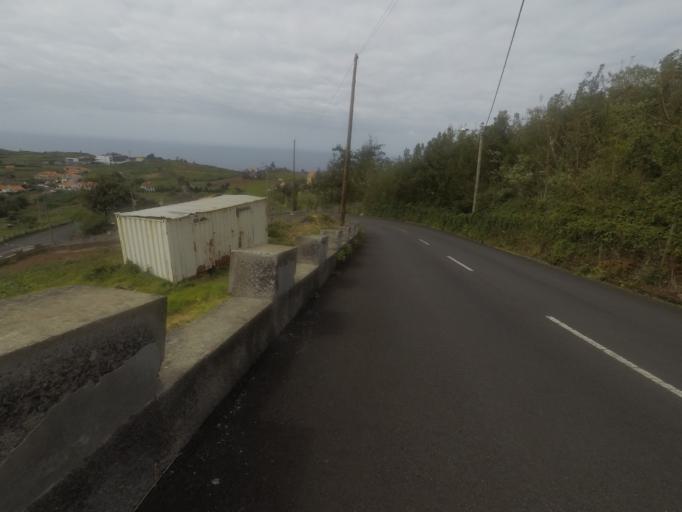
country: PT
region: Madeira
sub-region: Santana
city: Santana
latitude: 32.8207
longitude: -16.8855
